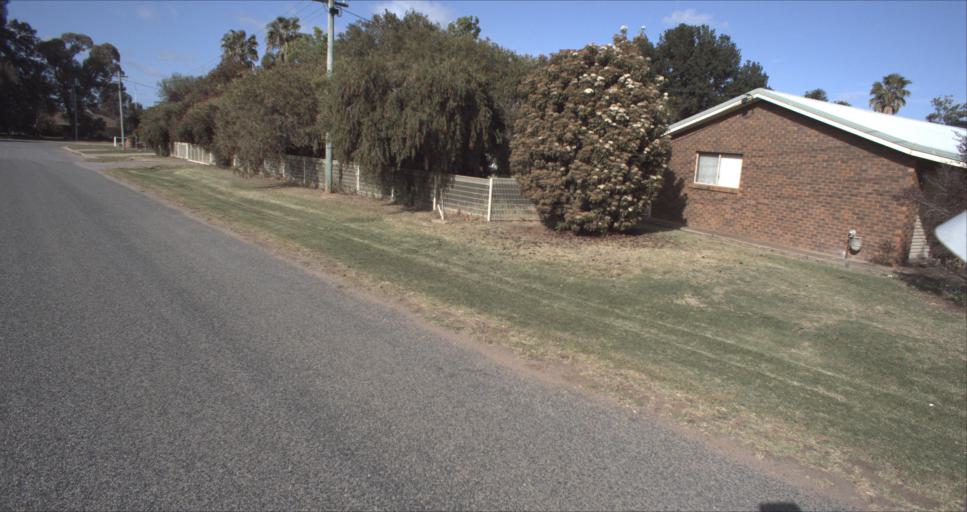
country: AU
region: New South Wales
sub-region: Leeton
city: Leeton
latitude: -34.5689
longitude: 146.3919
